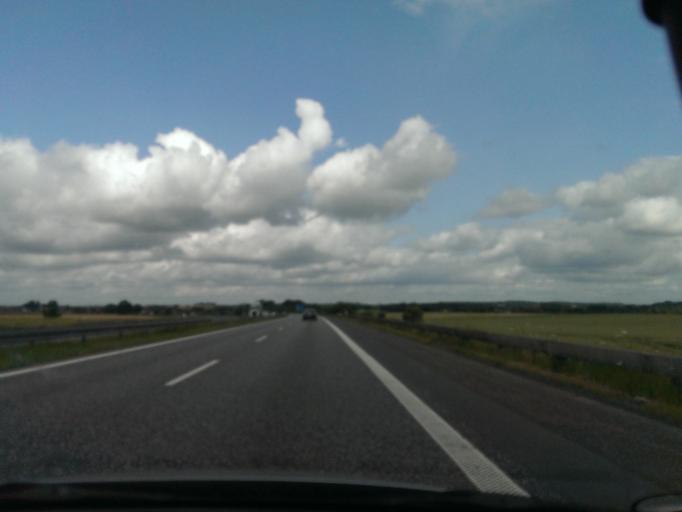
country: DK
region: Central Jutland
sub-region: Randers Kommune
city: Spentrup
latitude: 56.5331
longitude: 9.9273
